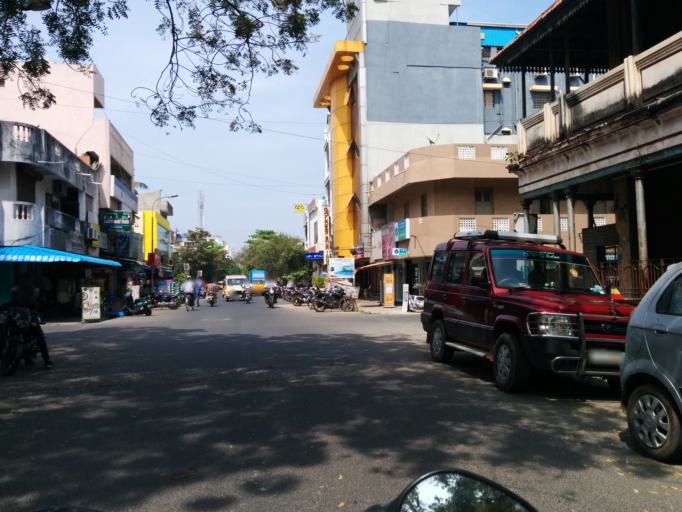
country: IN
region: Pondicherry
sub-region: Puducherry
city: Puducherry
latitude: 11.9390
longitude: 79.8317
